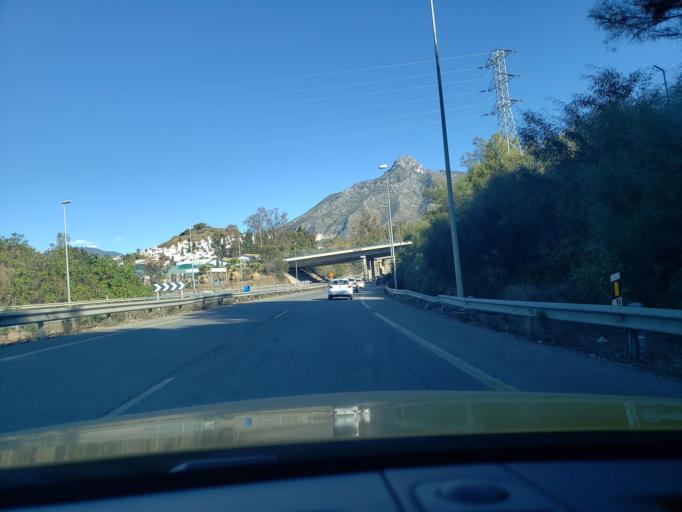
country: ES
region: Andalusia
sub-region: Provincia de Malaga
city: Marbella
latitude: 36.5096
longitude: -4.9482
